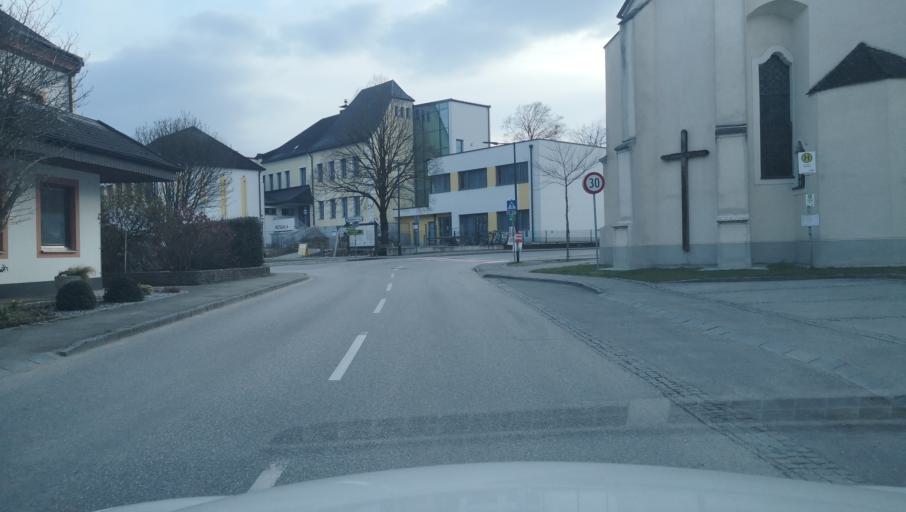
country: AT
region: Lower Austria
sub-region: Politischer Bezirk Amstetten
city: Winklarn
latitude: 48.0920
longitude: 14.8483
